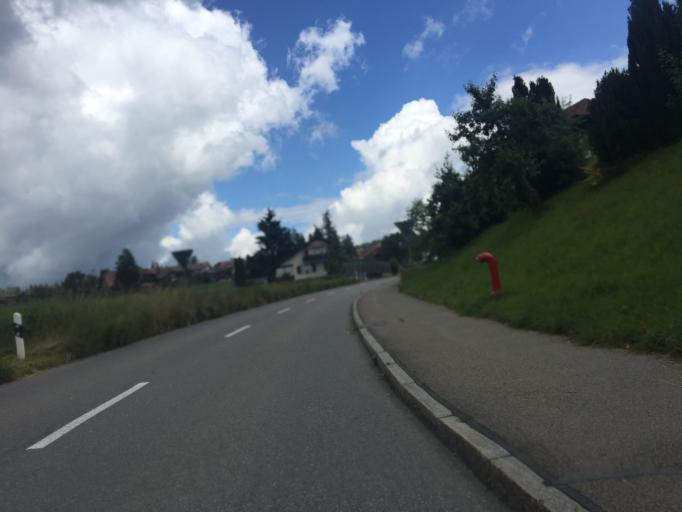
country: CH
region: Bern
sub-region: Bern-Mittelland District
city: Wohlen
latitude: 46.9721
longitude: 7.3562
